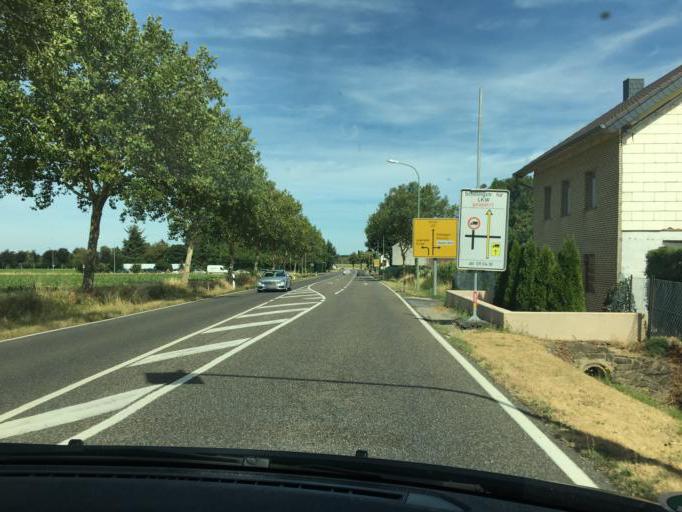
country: DE
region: North Rhine-Westphalia
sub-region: Regierungsbezirk Koln
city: Kreuzau
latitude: 50.7731
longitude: 6.4553
